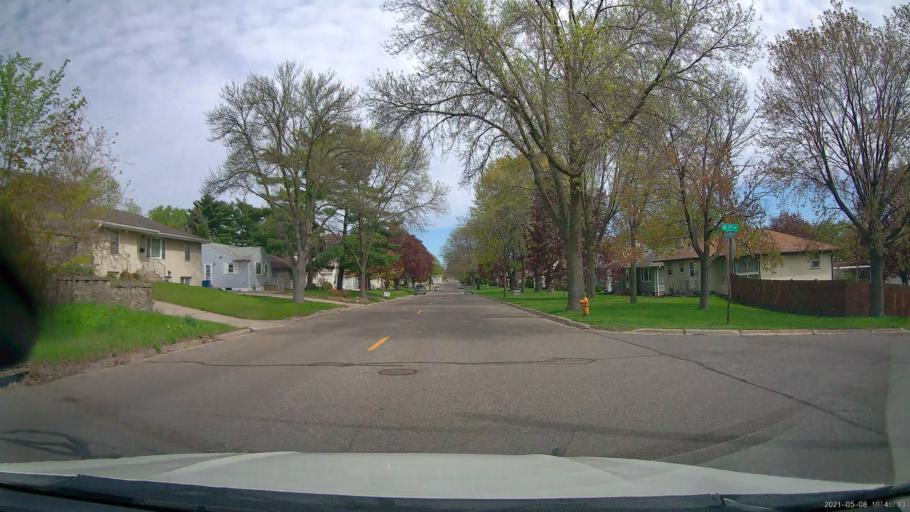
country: US
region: Minnesota
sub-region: Dakota County
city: South Saint Paul
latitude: 44.8924
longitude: -93.0526
